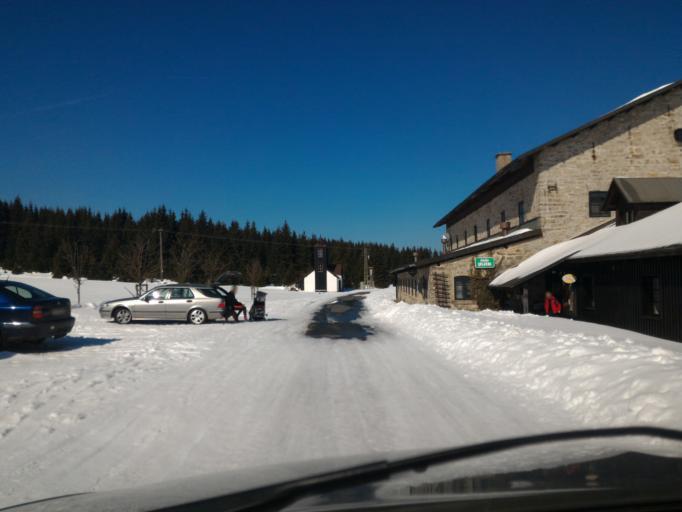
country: CZ
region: Liberecky
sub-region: Okres Jablonec nad Nisou
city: Korenov
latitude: 50.8187
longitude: 15.3448
